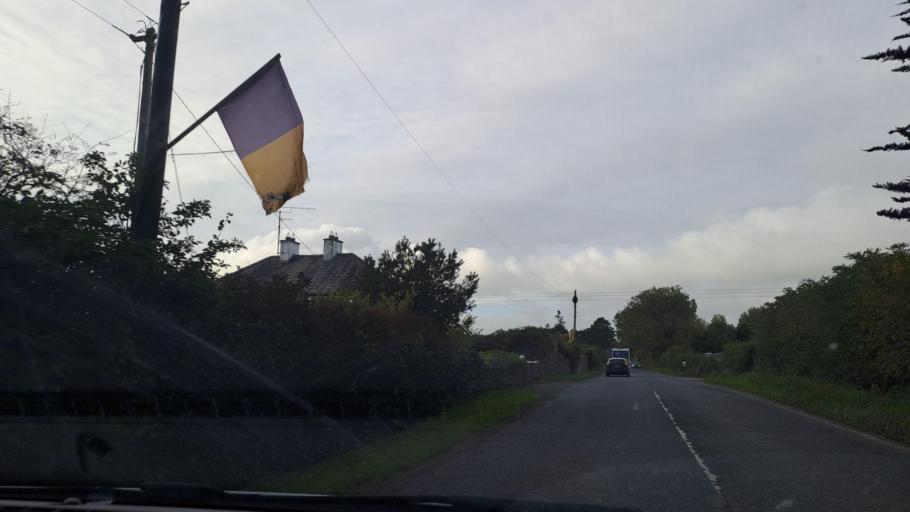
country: IE
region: Leinster
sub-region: An Mhi
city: Navan
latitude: 53.7089
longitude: -6.6881
